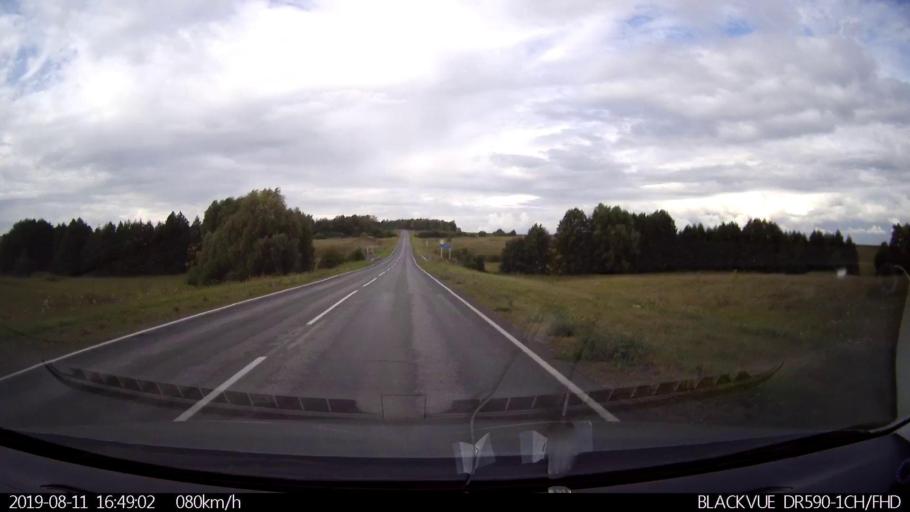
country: RU
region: Ulyanovsk
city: Mayna
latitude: 54.2163
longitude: 47.6945
